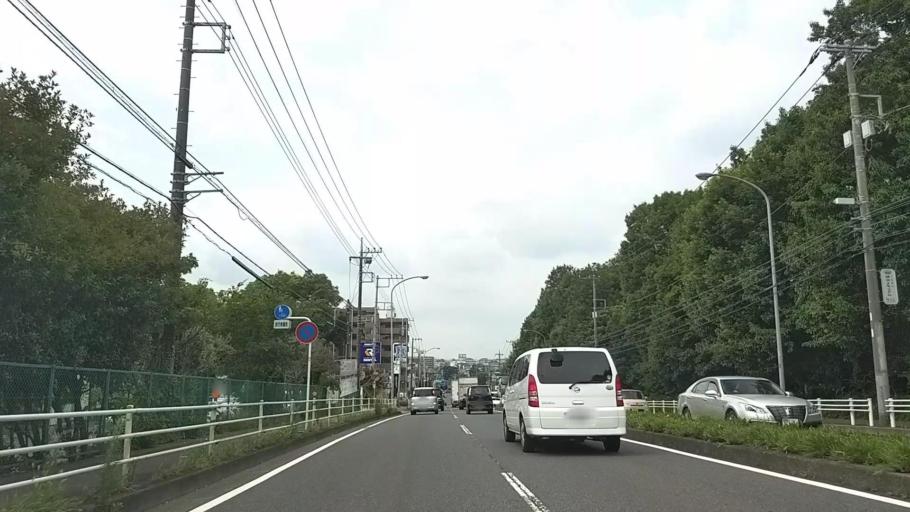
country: JP
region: Kanagawa
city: Minami-rinkan
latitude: 35.4736
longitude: 139.5003
